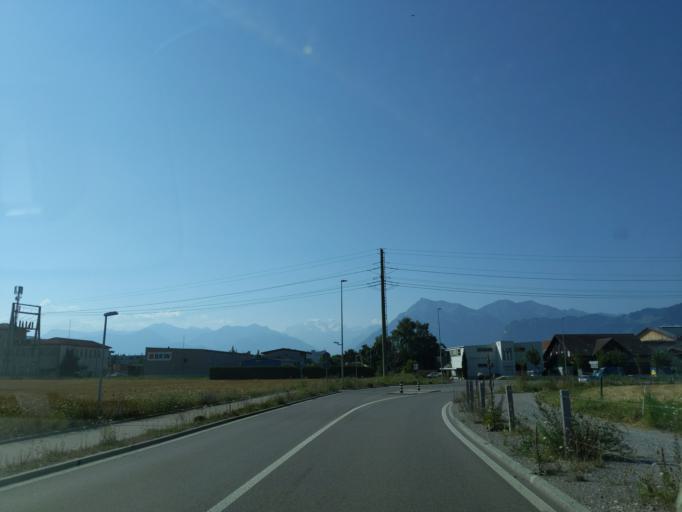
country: CH
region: Bern
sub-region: Thun District
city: Thun
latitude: 46.7691
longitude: 7.6150
